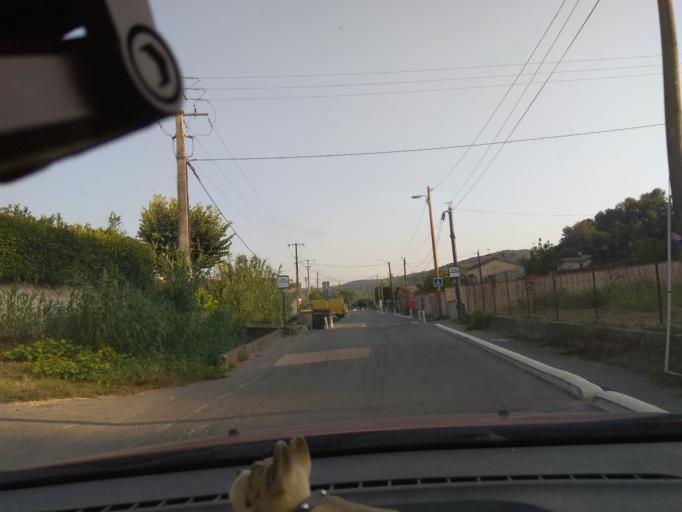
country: FR
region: Provence-Alpes-Cote d'Azur
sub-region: Departement des Alpes-Maritimes
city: La Colle-sur-Loup
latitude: 43.6806
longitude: 7.1068
